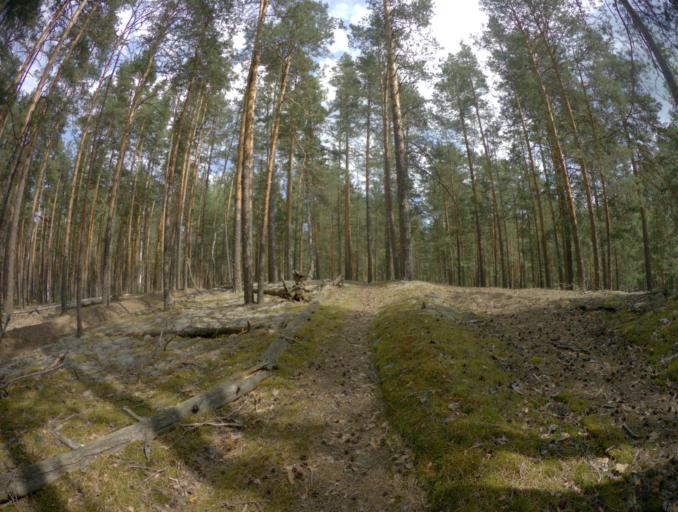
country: RU
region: Ivanovo
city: Talitsy
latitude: 56.3950
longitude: 42.3591
